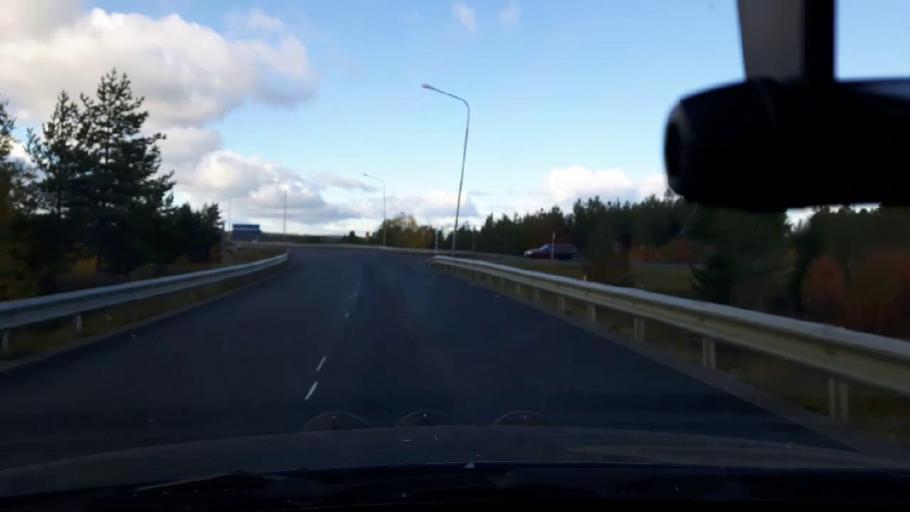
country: SE
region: Jaemtland
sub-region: Bergs Kommun
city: Hoverberg
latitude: 62.9748
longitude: 14.4835
